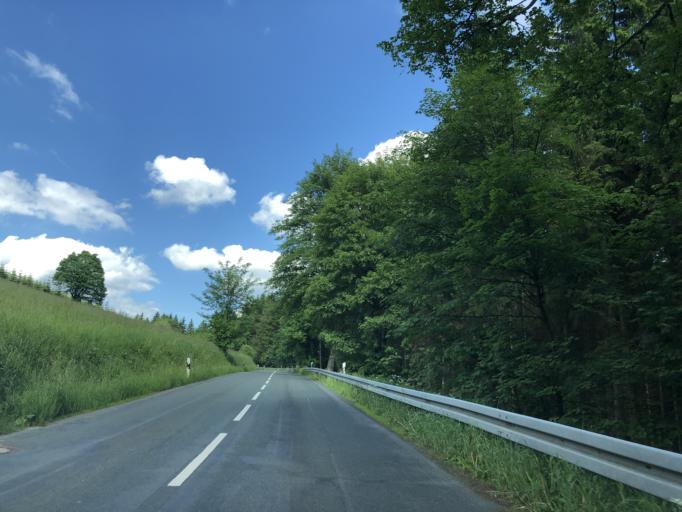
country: DE
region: North Rhine-Westphalia
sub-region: Regierungsbezirk Arnsberg
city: Winterberg
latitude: 51.1920
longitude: 8.4577
